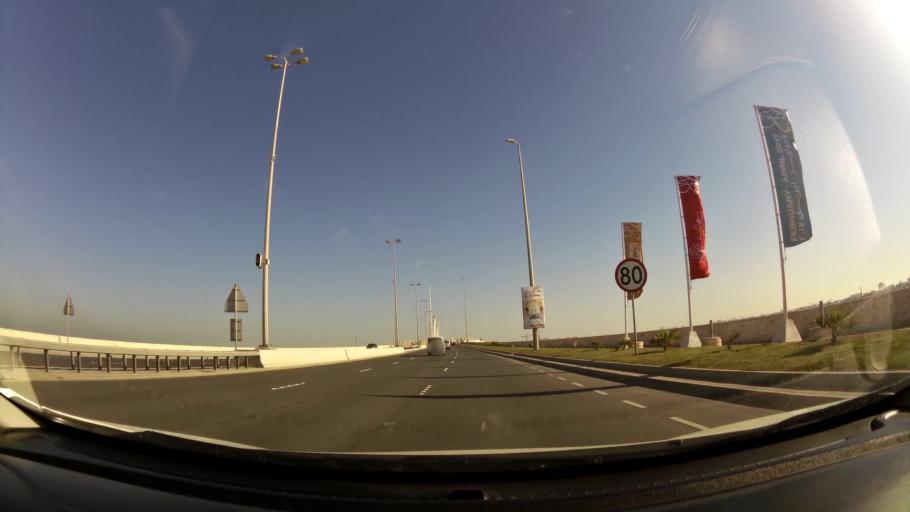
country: BH
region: Muharraq
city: Al Muharraq
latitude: 26.2505
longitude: 50.5926
